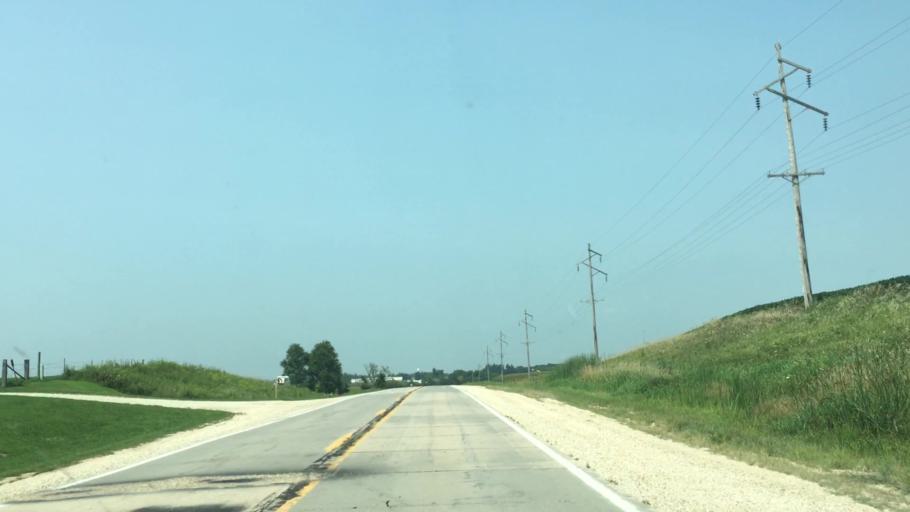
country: US
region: Iowa
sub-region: Winneshiek County
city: Decorah
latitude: 43.1487
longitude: -91.8643
